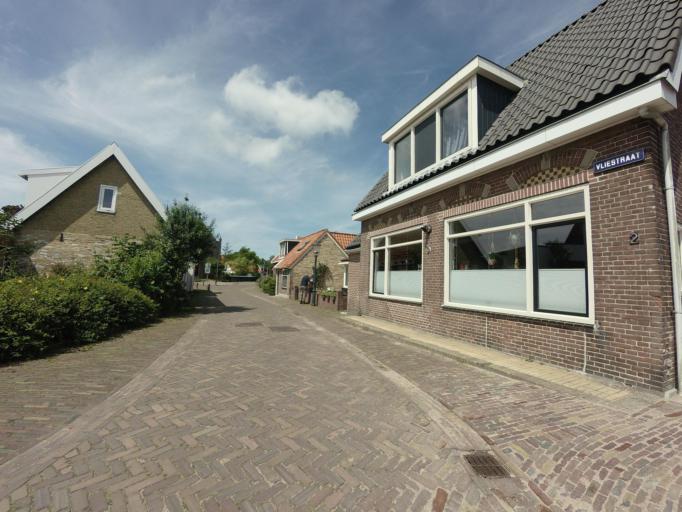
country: NL
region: North Holland
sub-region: Gemeente Texel
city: Den Burg
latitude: 53.0847
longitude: 4.8725
